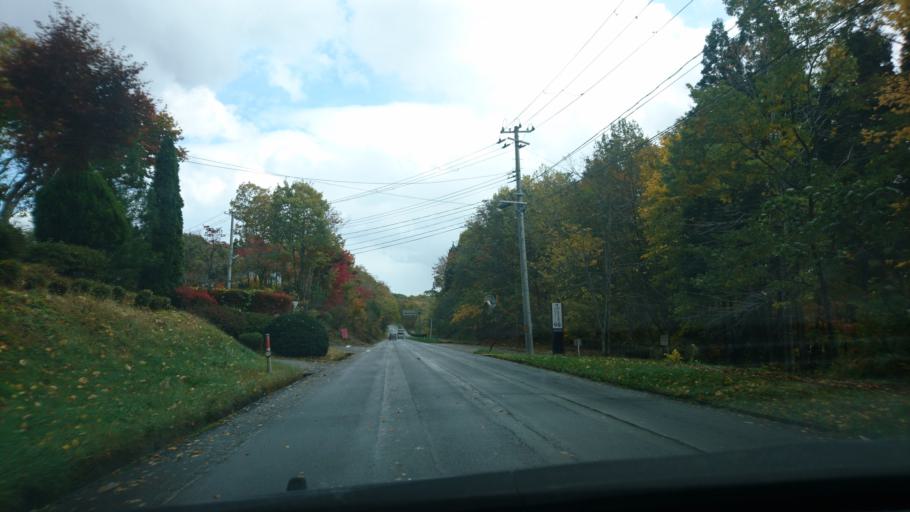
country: JP
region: Iwate
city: Shizukuishi
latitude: 39.6761
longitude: 141.0000
